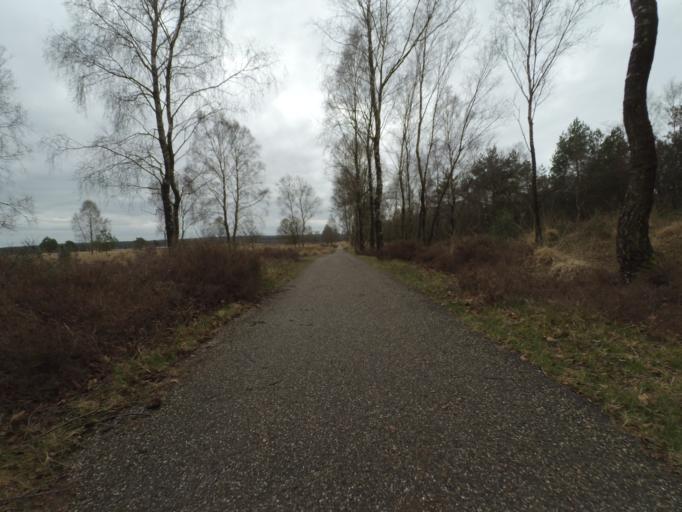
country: NL
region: Gelderland
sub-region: Gemeente Rozendaal
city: Rozendaal
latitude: 52.0382
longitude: 5.9383
